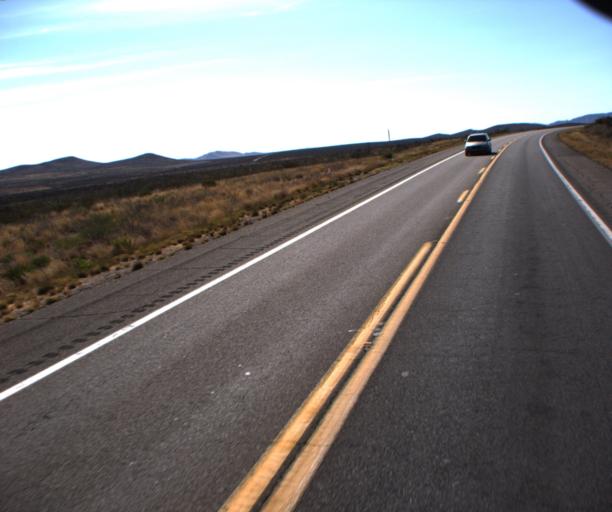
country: US
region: Arizona
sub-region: Cochise County
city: Tombstone
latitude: 31.6899
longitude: -110.0367
